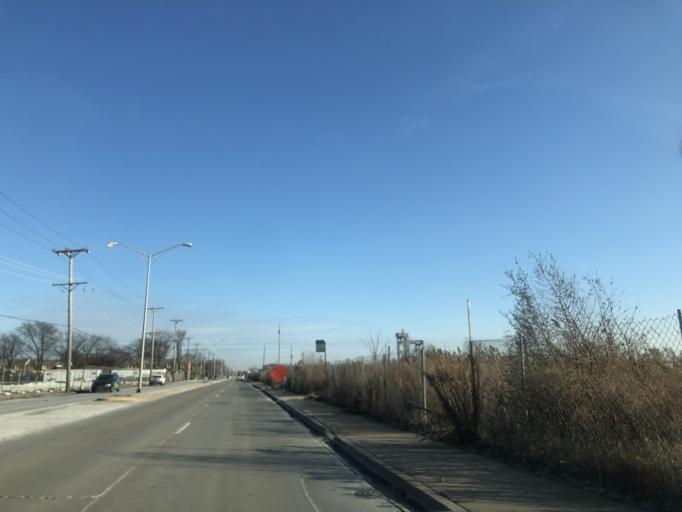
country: US
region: Illinois
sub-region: Cook County
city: Burbank
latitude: 41.7744
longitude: -87.7595
